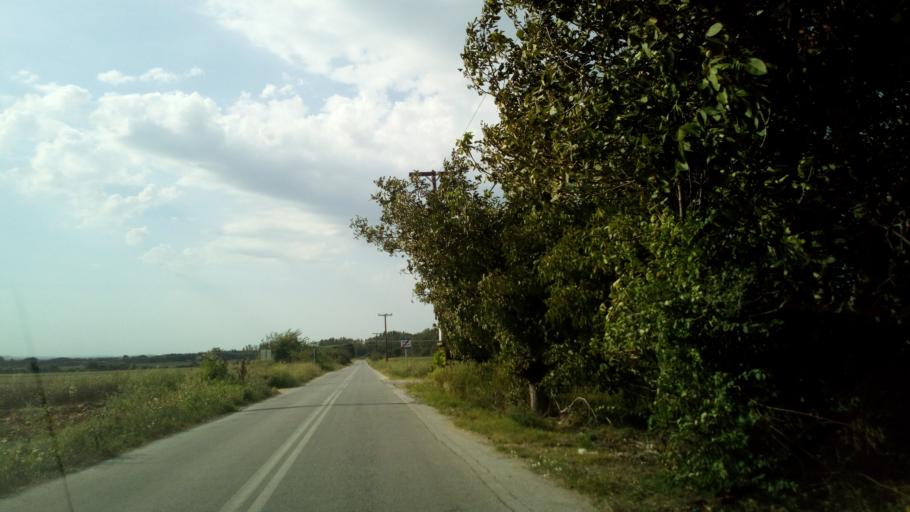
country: GR
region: Central Macedonia
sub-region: Nomos Chalkidikis
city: Galatista
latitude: 40.5594
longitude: 23.2974
